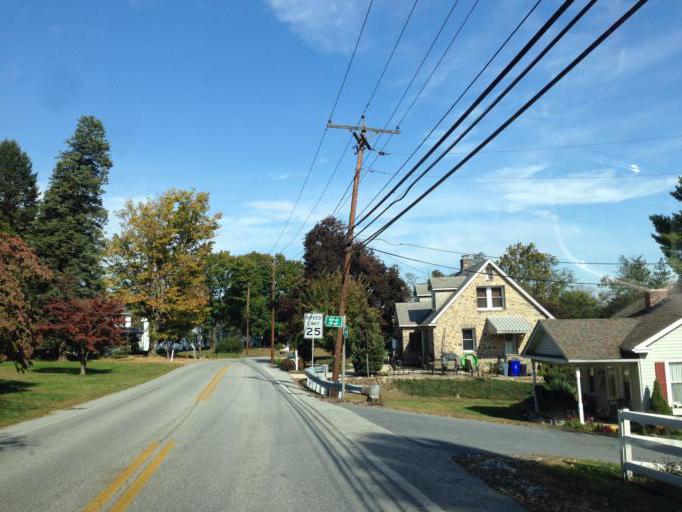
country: US
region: Maryland
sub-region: Howard County
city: Ellicott City
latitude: 39.2643
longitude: -76.8049
